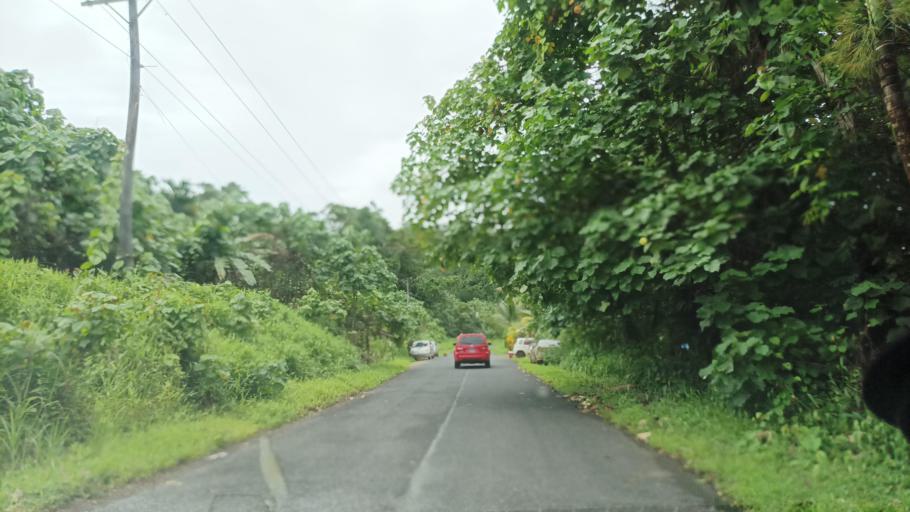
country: FM
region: Pohnpei
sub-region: Madolenihm Municipality
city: Madolenihm Municipality Government
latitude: 6.8960
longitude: 158.3081
